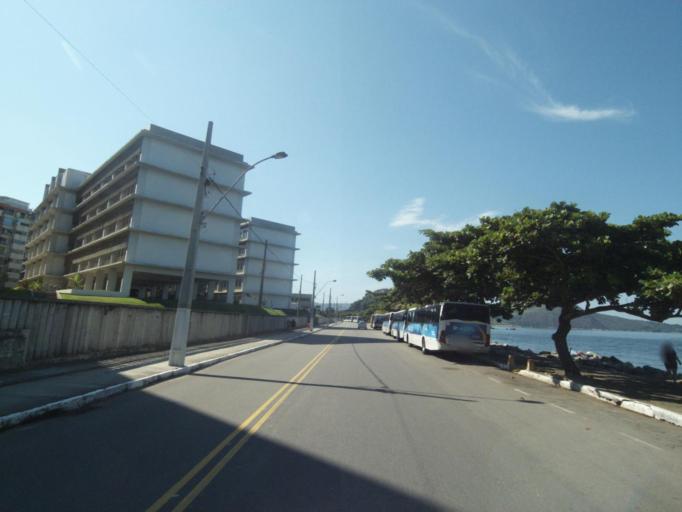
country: BR
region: Rio de Janeiro
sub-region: Niteroi
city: Niteroi
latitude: -22.9060
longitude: -43.1345
